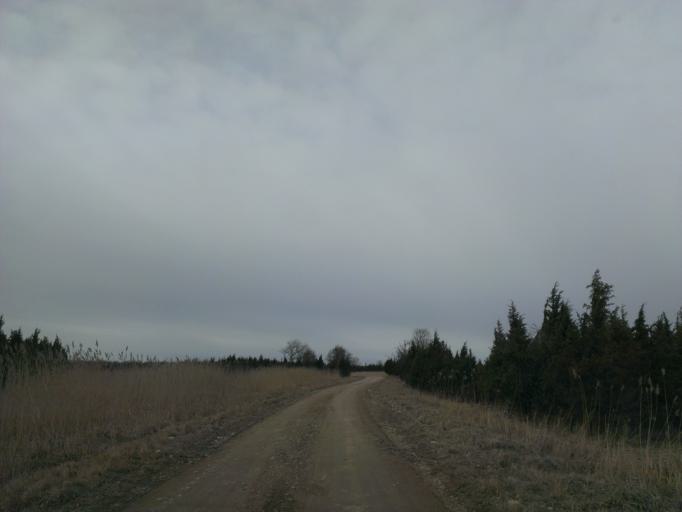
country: EE
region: Laeaene
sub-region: Lihula vald
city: Lihula
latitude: 58.5636
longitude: 23.5488
